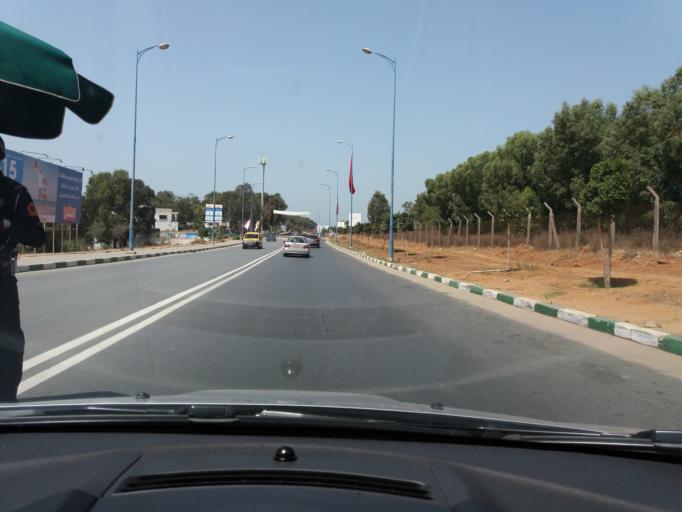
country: MA
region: Gharb-Chrarda-Beni Hssen
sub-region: Kenitra Province
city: Kenitra
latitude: 34.2704
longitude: -6.6389
